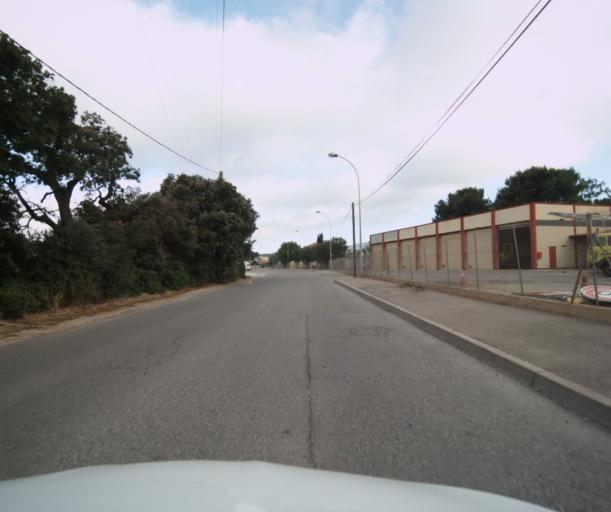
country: FR
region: Provence-Alpes-Cote d'Azur
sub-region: Departement du Var
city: Ollioules
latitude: 43.1189
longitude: 5.8517
